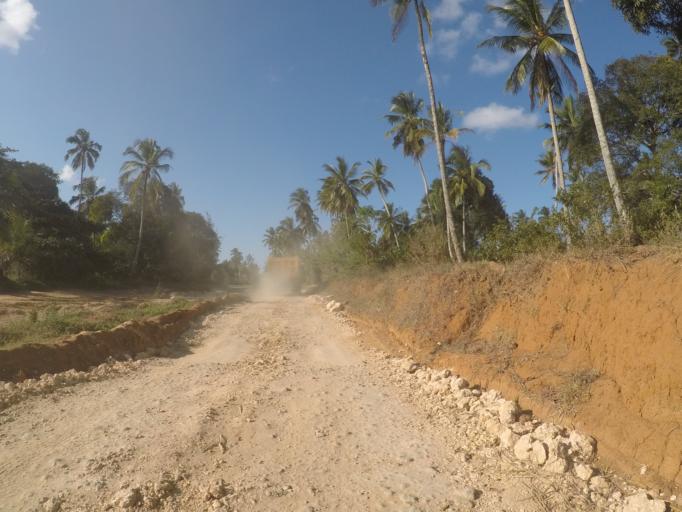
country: TZ
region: Zanzibar Central/South
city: Koani
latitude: -6.1723
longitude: 39.2851
